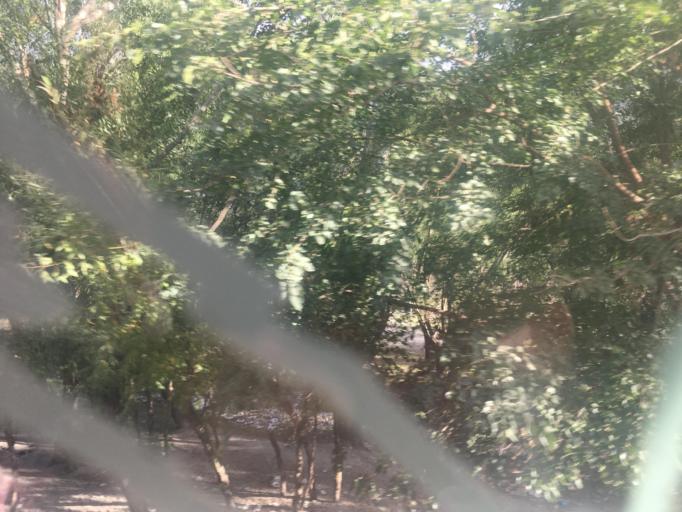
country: PK
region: Gilgit-Baltistan
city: Skardu
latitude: 35.3002
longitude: 75.6286
